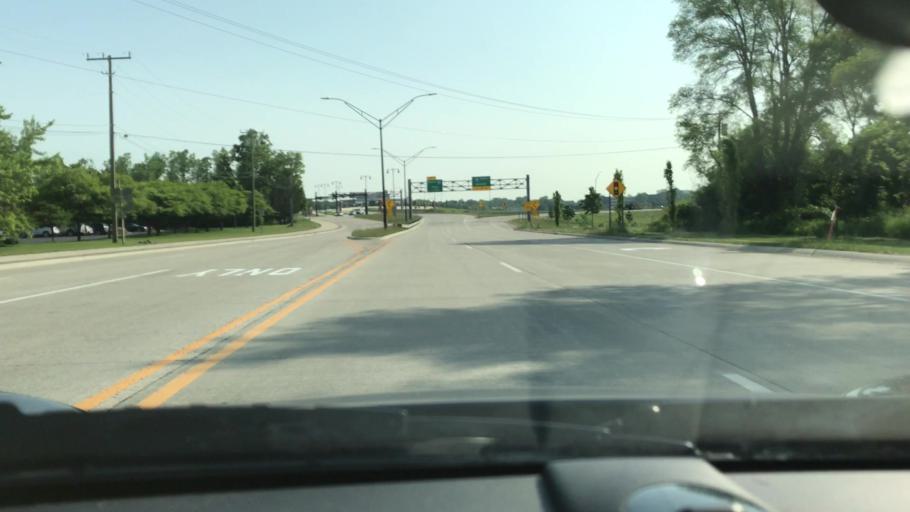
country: US
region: Michigan
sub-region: Oakland County
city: Auburn Hills
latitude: 42.6627
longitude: -83.2448
